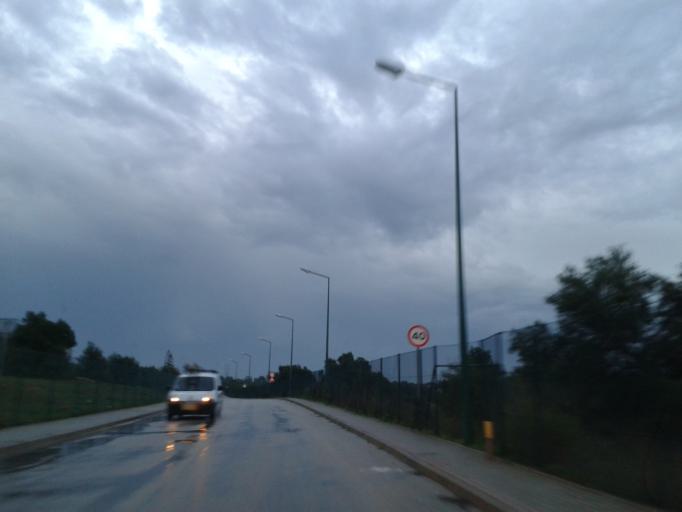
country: PT
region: Faro
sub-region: Lagoa
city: Estombar
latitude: 37.1336
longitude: -8.4808
